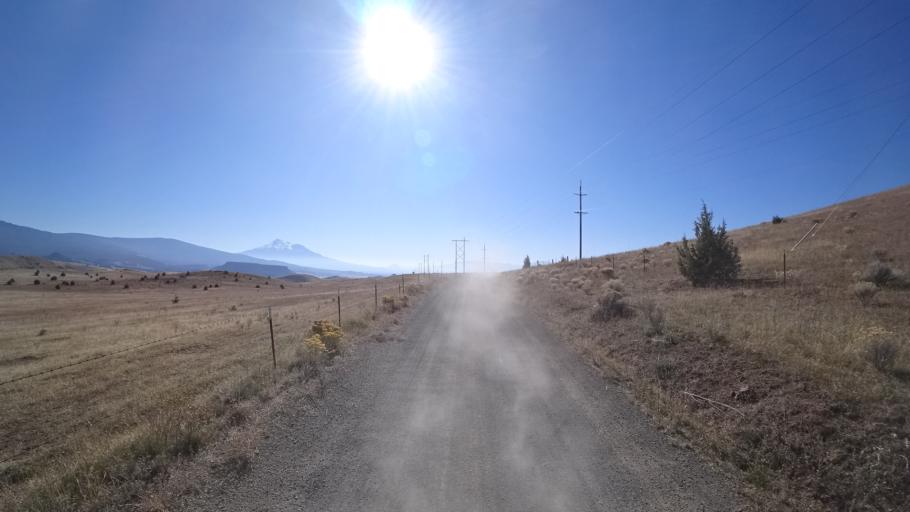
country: US
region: California
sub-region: Siskiyou County
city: Montague
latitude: 41.7742
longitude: -122.3587
